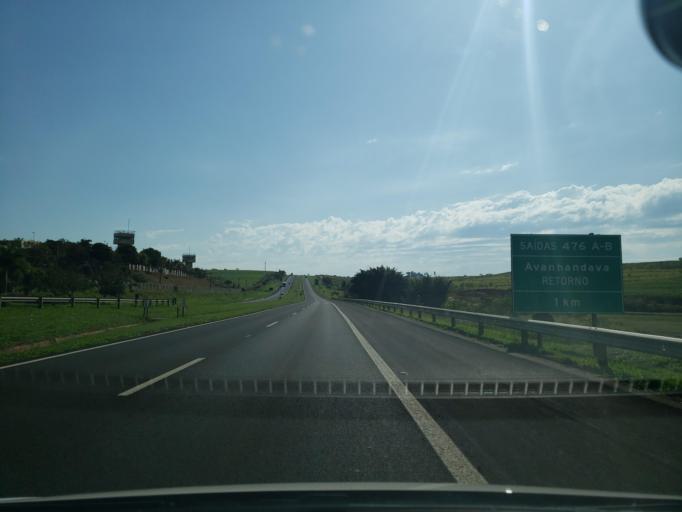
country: BR
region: Sao Paulo
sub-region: Penapolis
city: Penapolis
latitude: -21.5186
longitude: -50.0033
